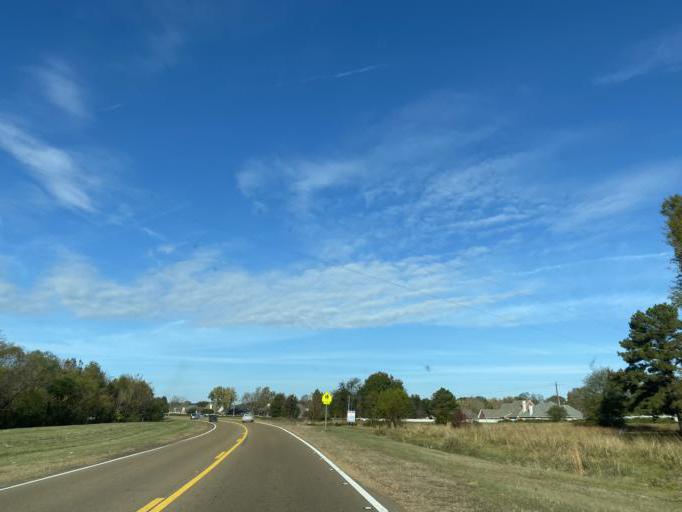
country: US
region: Mississippi
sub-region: Madison County
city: Madison
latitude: 32.4792
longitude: -90.1575
